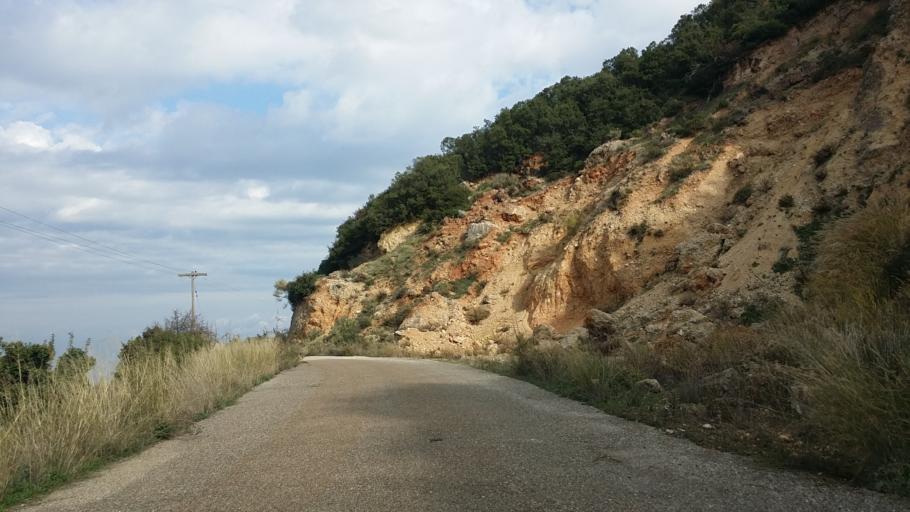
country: GR
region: West Greece
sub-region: Nomos Aitolias kai Akarnanias
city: Katouna
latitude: 38.8580
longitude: 21.0561
